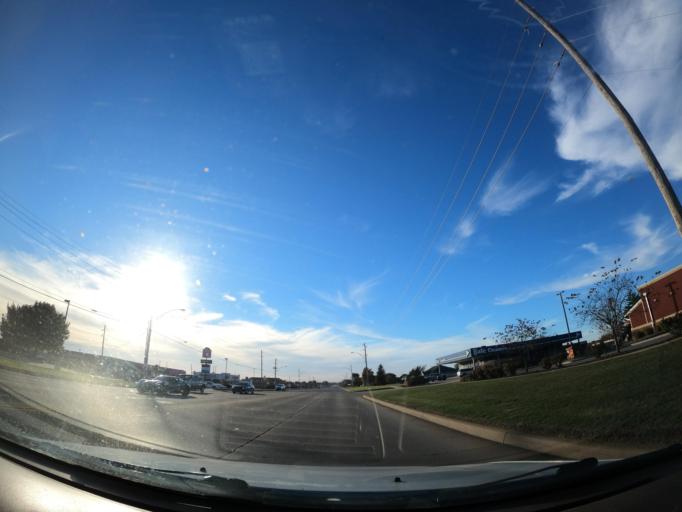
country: US
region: Oklahoma
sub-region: Tulsa County
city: Owasso
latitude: 36.2786
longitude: -95.8306
